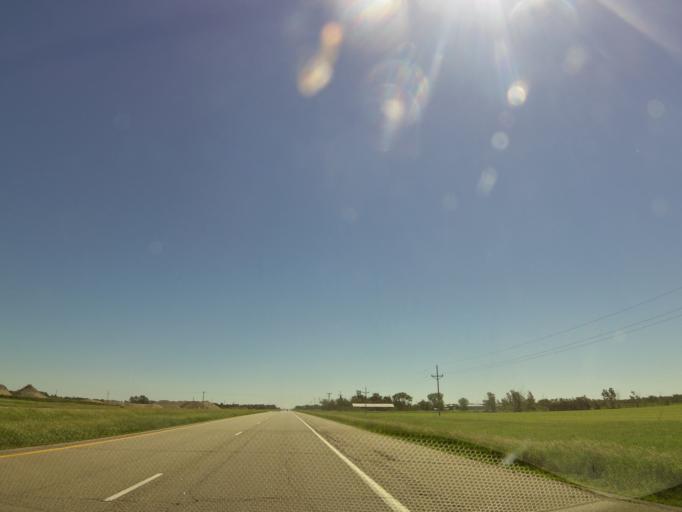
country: US
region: Minnesota
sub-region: Polk County
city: Crookston
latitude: 47.7603
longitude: -96.4432
